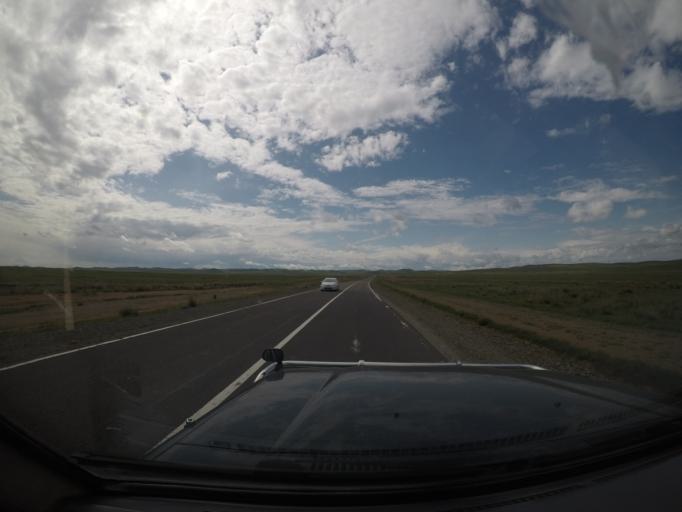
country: MN
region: Hentiy
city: Moron
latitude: 47.4178
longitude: 109.9081
